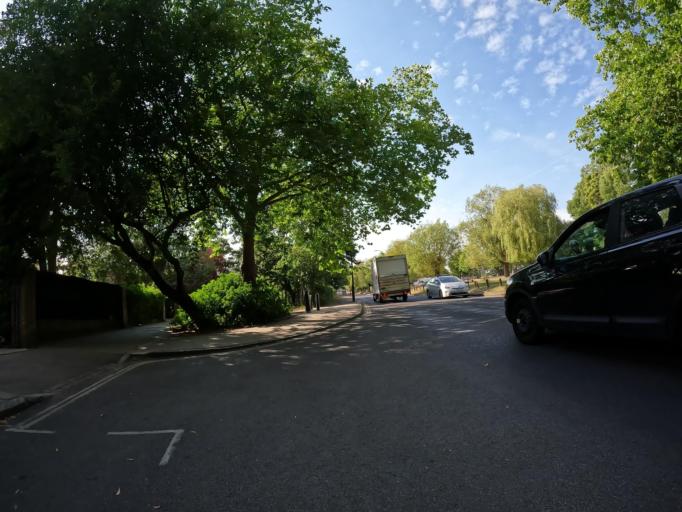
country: GB
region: England
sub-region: Greater London
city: Hadley Wood
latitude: 51.6622
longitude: -0.1710
